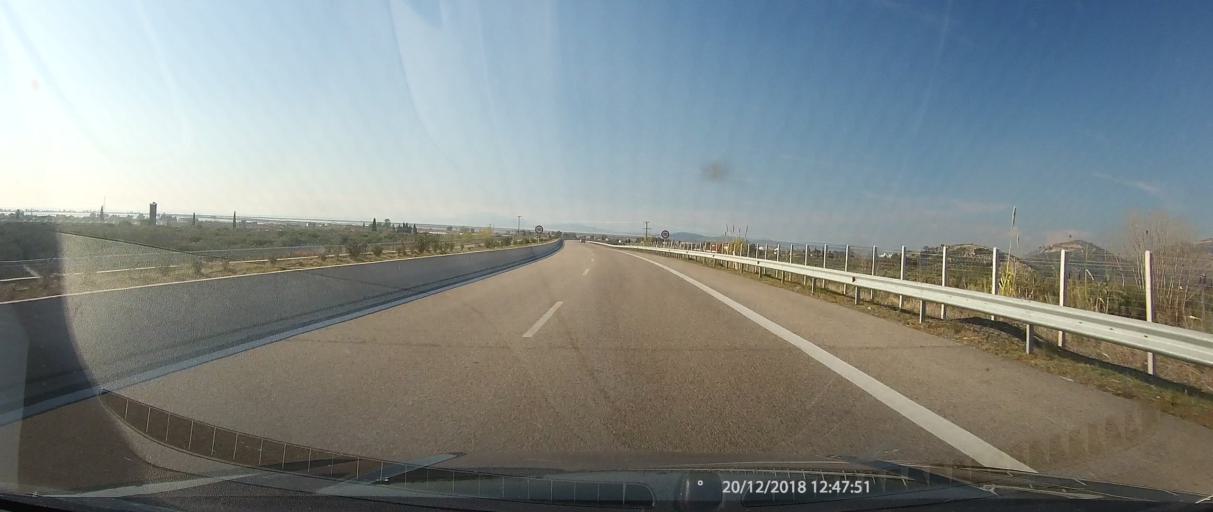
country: GR
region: West Greece
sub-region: Nomos Aitolias kai Akarnanias
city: Mesolongi
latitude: 38.3941
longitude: 21.4352
